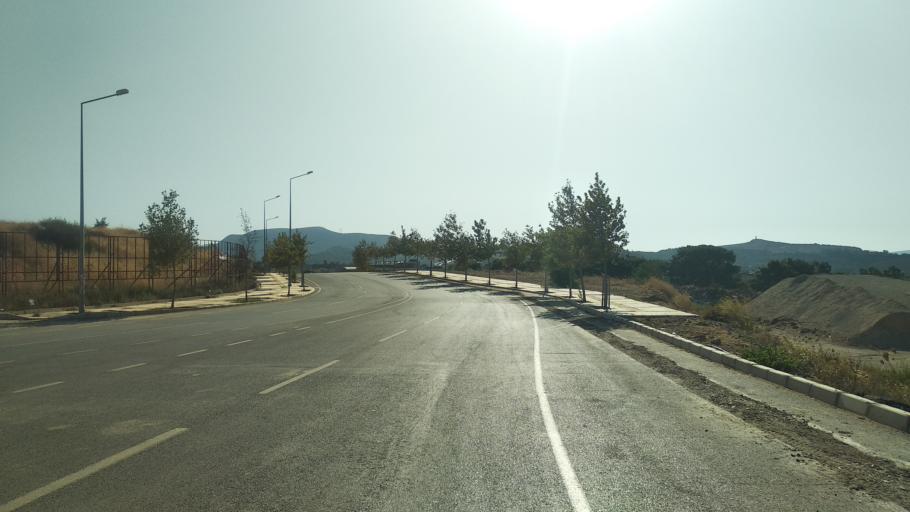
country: TR
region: Izmir
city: Urla
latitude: 38.3601
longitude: 26.8785
